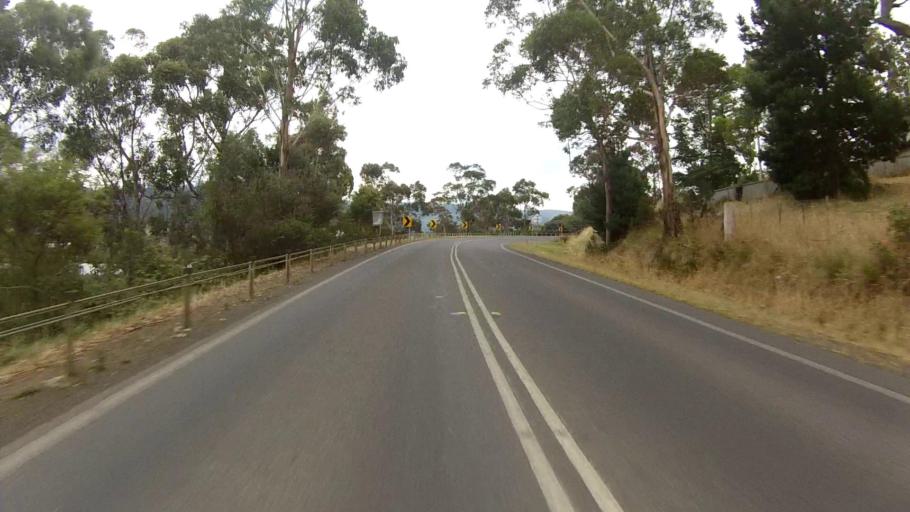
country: AU
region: Tasmania
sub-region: Huon Valley
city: Franklin
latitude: -43.0920
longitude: 147.0242
